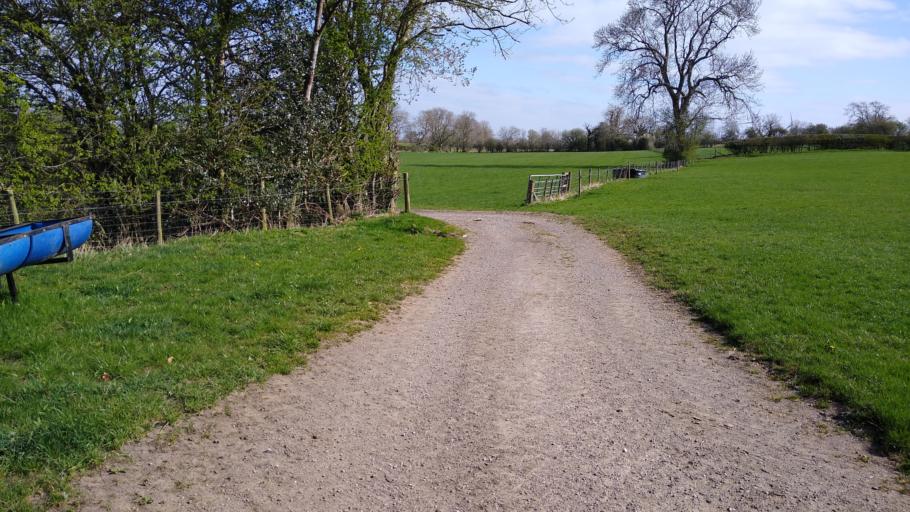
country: GB
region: England
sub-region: Cumbria
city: Dearham
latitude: 54.7132
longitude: -3.3983
